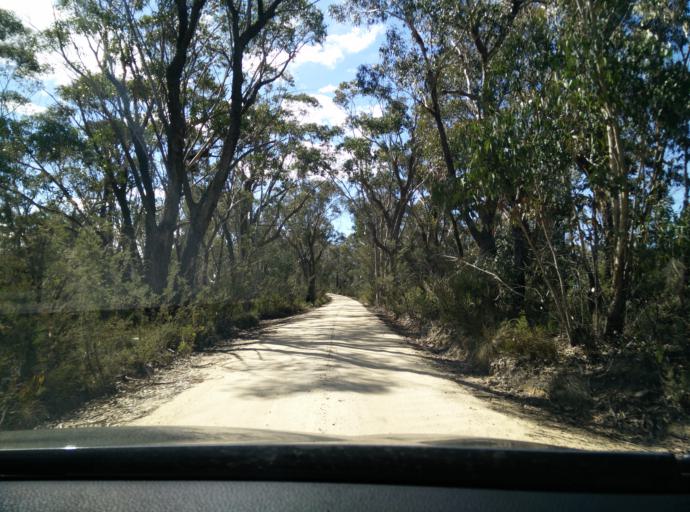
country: AU
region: New South Wales
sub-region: Blue Mountains Municipality
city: Blackheath
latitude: -33.5712
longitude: 150.2882
